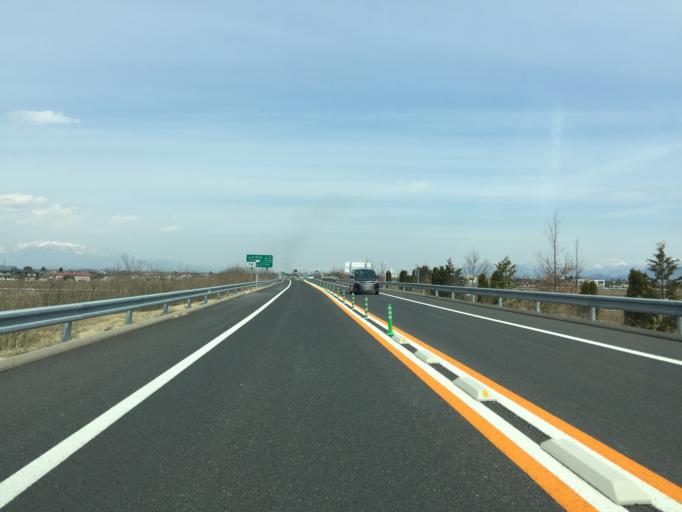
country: JP
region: Yamagata
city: Yamagata-shi
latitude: 38.2600
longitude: 140.2897
